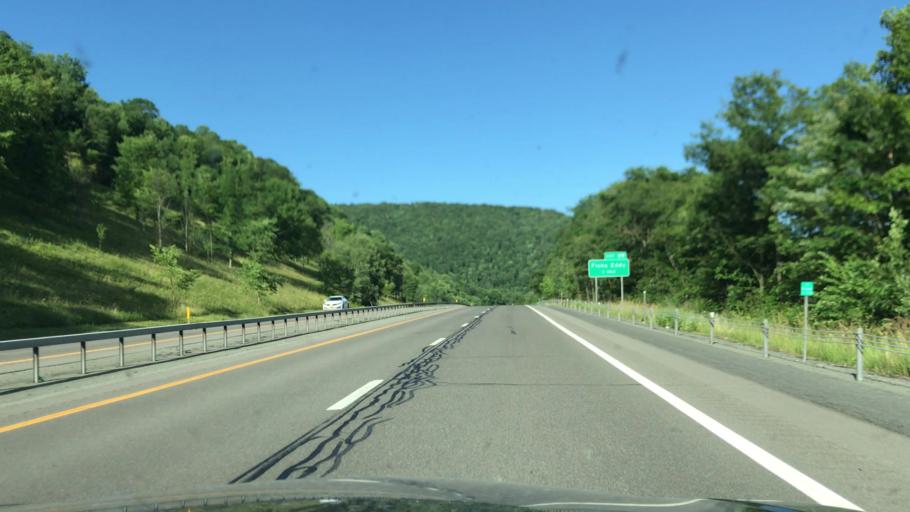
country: US
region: New York
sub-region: Delaware County
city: Hancock
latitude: 41.9751
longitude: -75.2082
